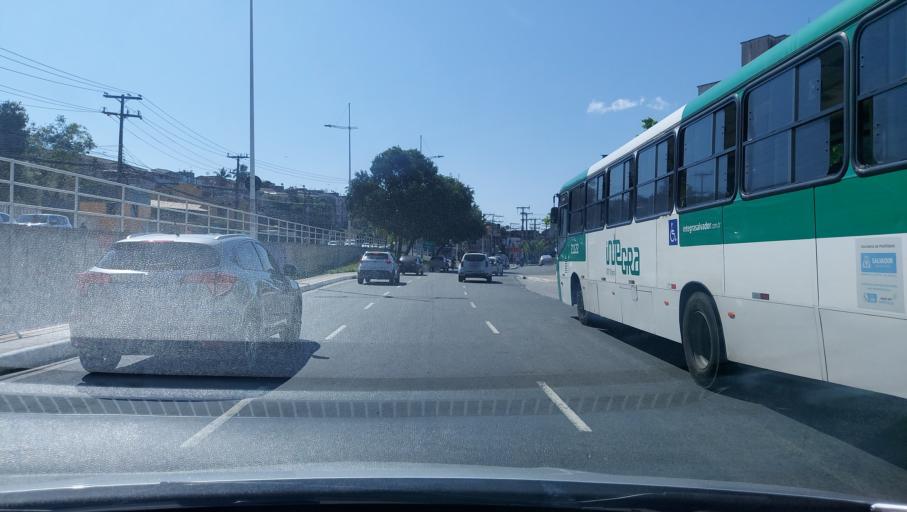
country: BR
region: Bahia
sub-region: Salvador
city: Salvador
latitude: -12.9612
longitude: -38.4386
